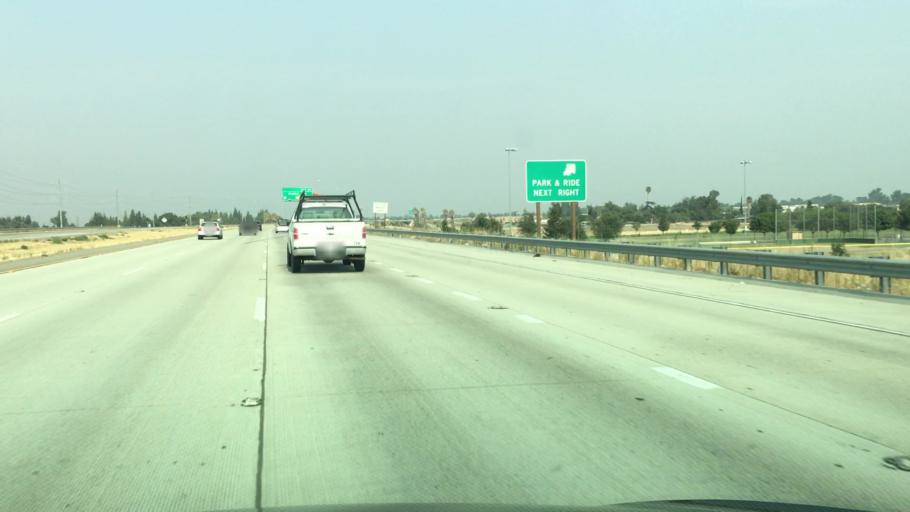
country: US
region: California
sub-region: Fresno County
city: Sunnyside
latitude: 36.7532
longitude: -119.6898
